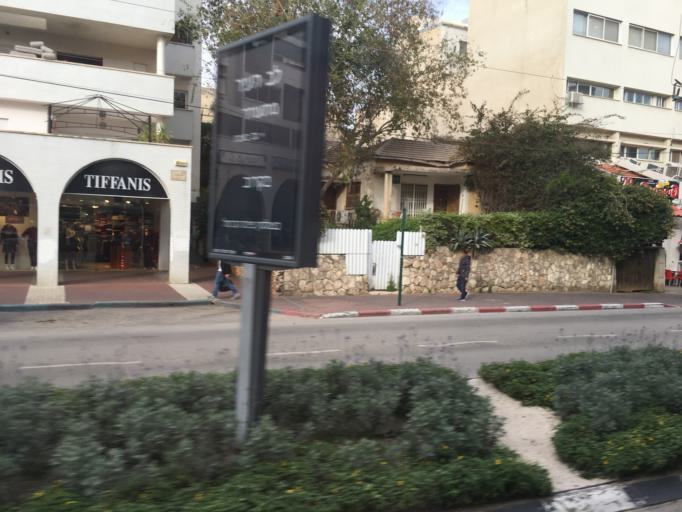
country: IL
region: Central District
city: Kfar Saba
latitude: 32.1768
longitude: 34.9017
